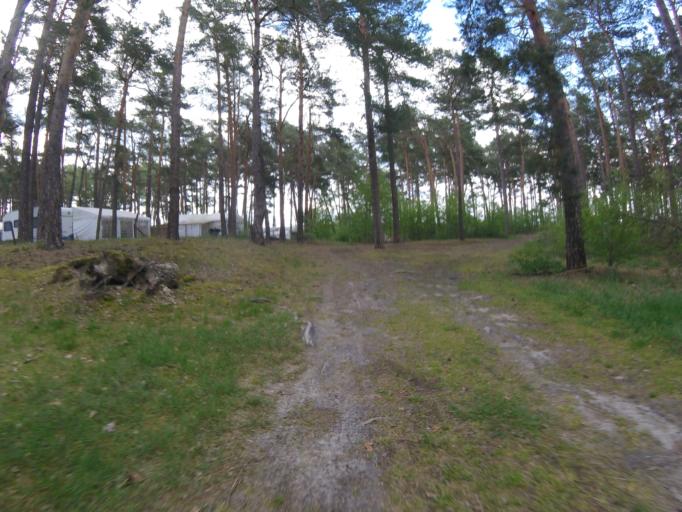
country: DE
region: Brandenburg
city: Schwerin
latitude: 52.1527
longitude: 13.6085
